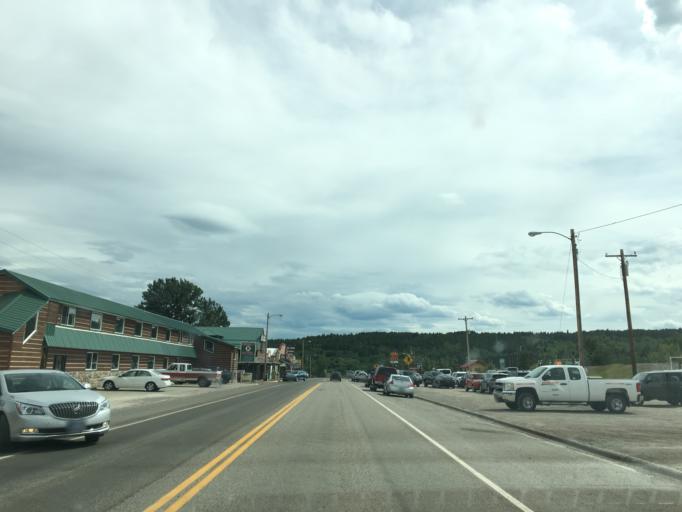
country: US
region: Montana
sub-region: Glacier County
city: South Browning
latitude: 48.4428
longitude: -113.2182
